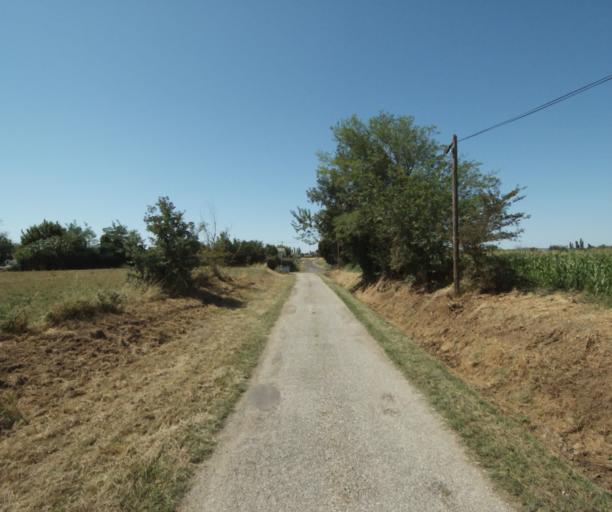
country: FR
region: Midi-Pyrenees
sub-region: Departement de la Haute-Garonne
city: Revel
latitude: 43.4744
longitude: 1.9853
